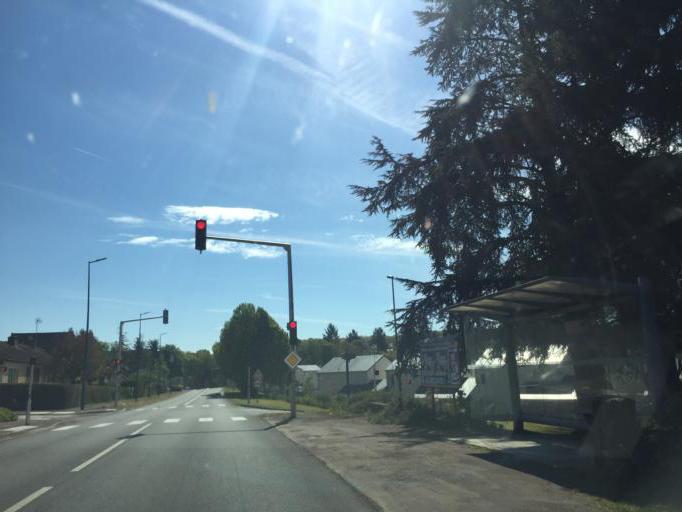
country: FR
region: Bourgogne
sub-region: Departement de la Nievre
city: Clamecy
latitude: 47.4555
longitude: 3.5323
